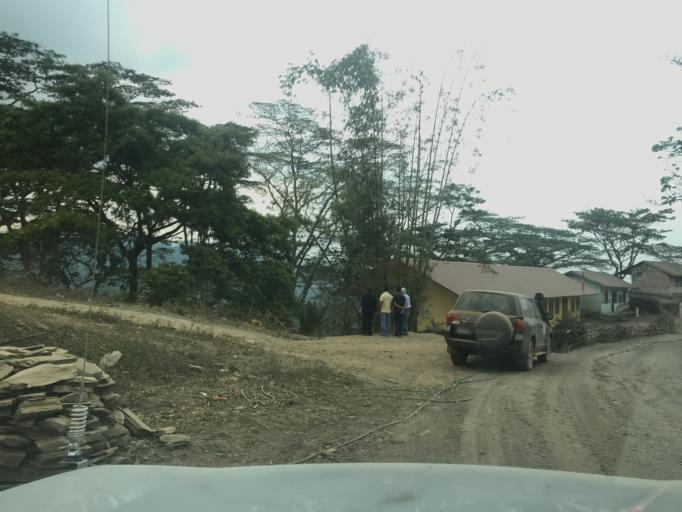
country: TL
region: Ermera
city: Gleno
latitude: -8.7600
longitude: 125.4300
